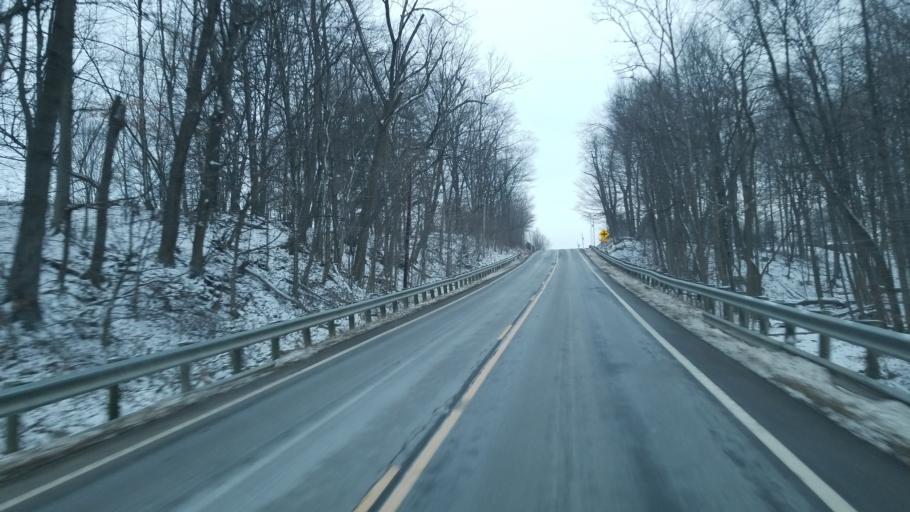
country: US
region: Ohio
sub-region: Ashland County
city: Loudonville
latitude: 40.7575
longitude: -82.2599
